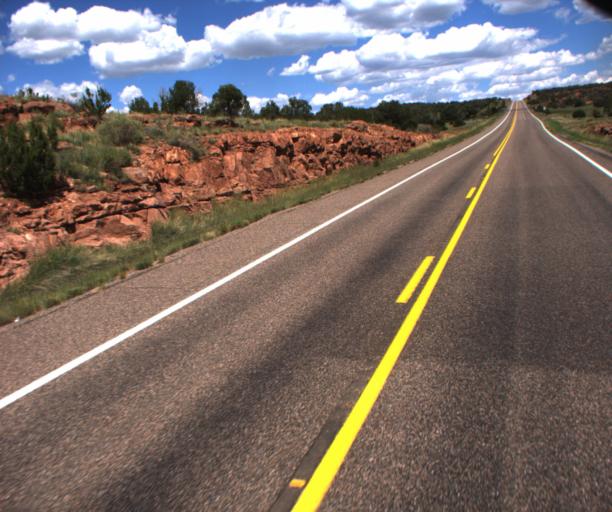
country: US
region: Arizona
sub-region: Apache County
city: Springerville
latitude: 34.1568
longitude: -109.1184
